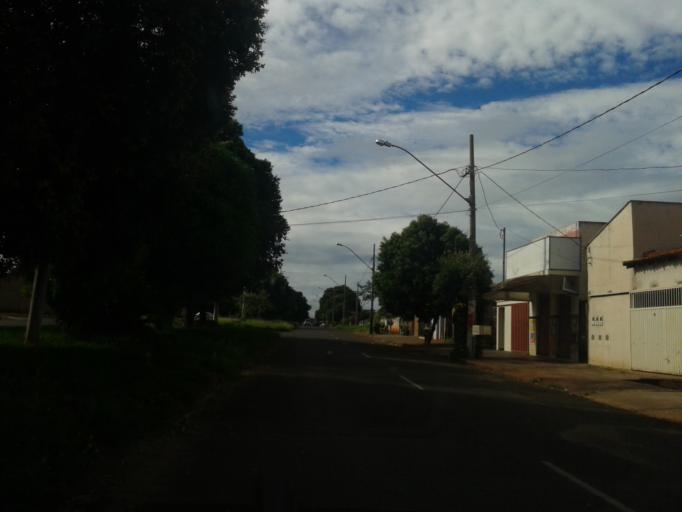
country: BR
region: Minas Gerais
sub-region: Ituiutaba
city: Ituiutaba
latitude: -18.9891
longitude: -49.4678
